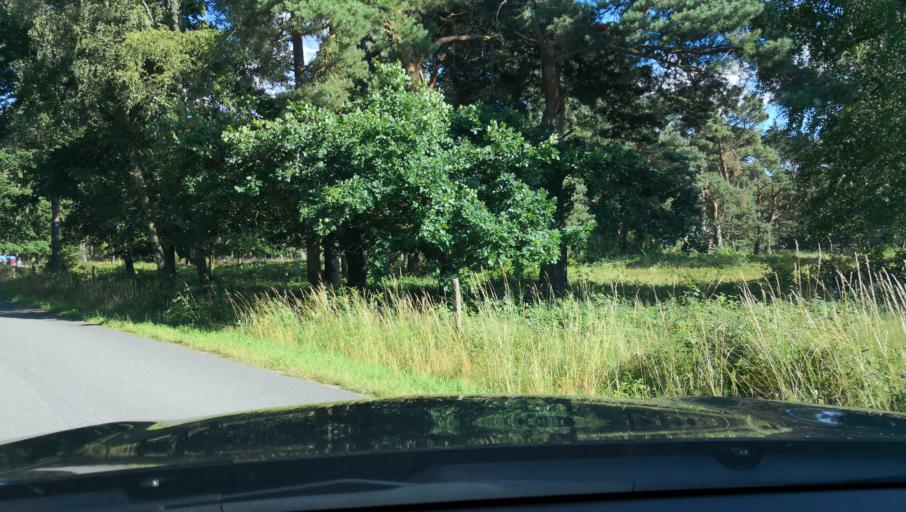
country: SE
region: Skane
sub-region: Simrishamns Kommun
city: Kivik
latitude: 55.7897
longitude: 14.1958
